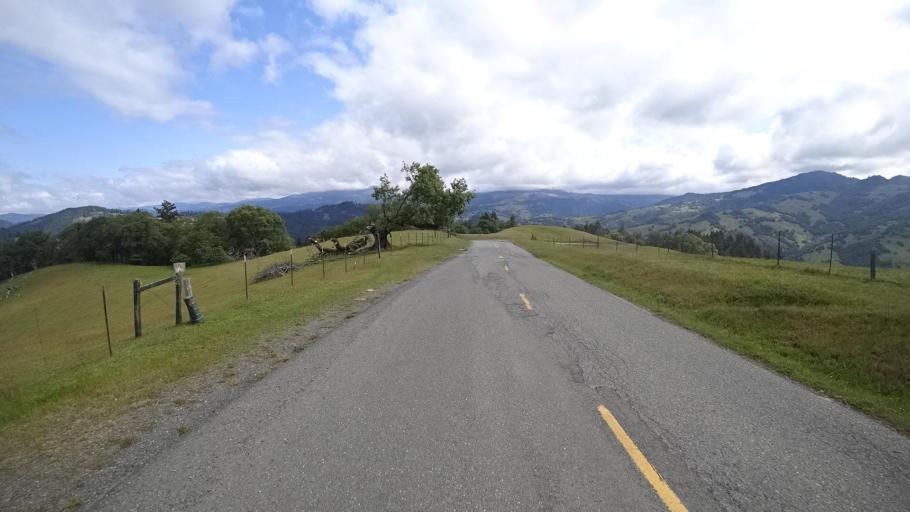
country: US
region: California
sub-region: Humboldt County
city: Redway
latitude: 40.1568
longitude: -123.6217
